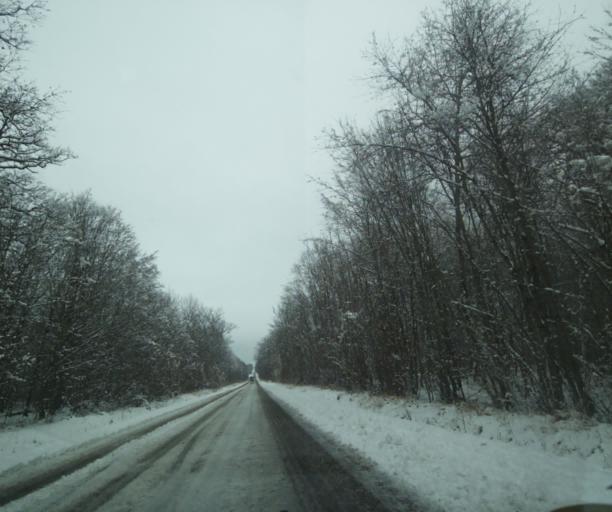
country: FR
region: Champagne-Ardenne
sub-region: Departement de la Haute-Marne
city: Montier-en-Der
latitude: 48.5180
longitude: 4.7473
